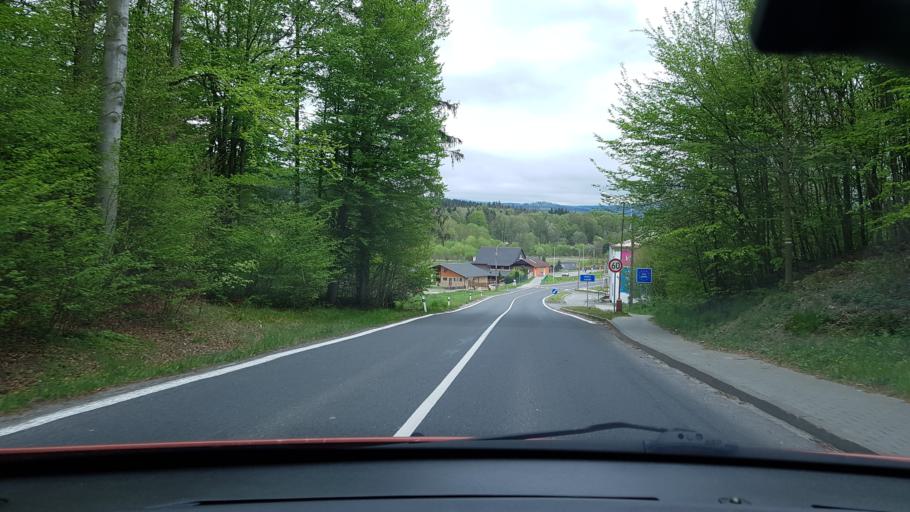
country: CZ
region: Olomoucky
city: Mikulovice
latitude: 50.3109
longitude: 17.3500
